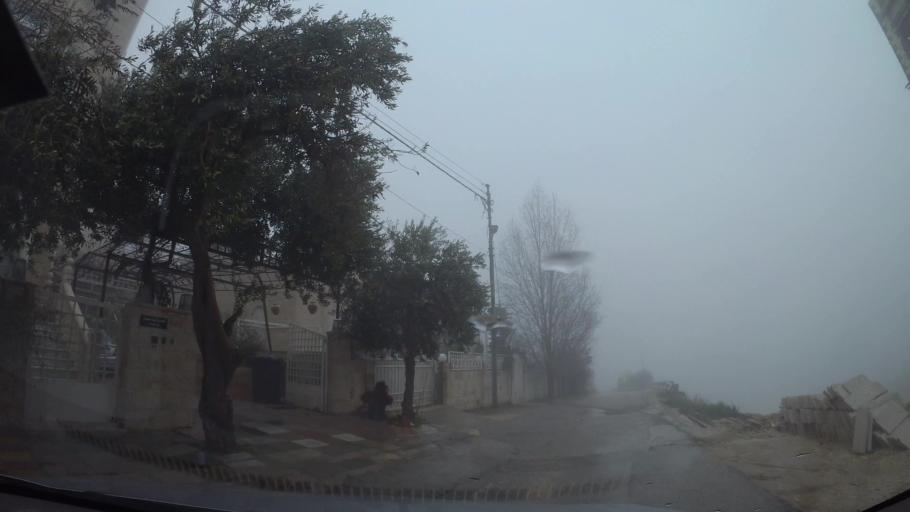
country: JO
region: Amman
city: Al Jubayhah
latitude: 32.0037
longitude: 35.8923
